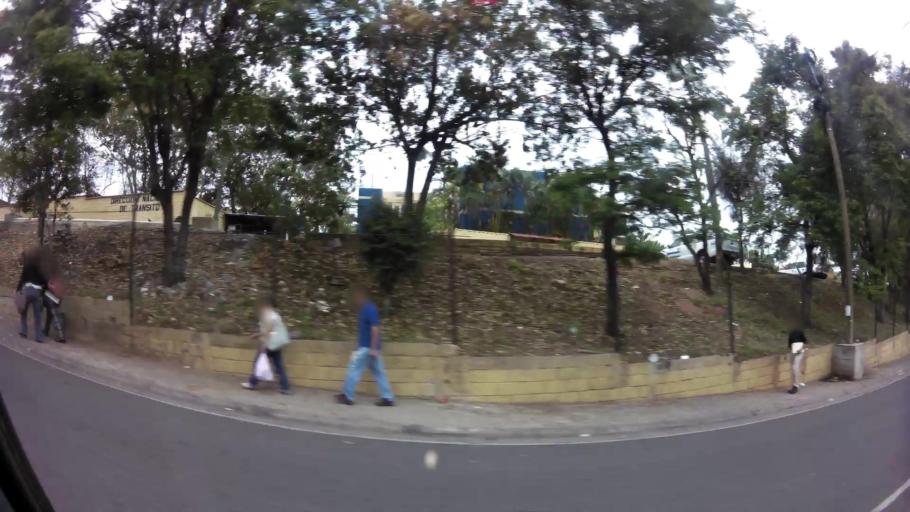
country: HN
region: Francisco Morazan
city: Tegucigalpa
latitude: 14.0751
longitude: -87.1830
